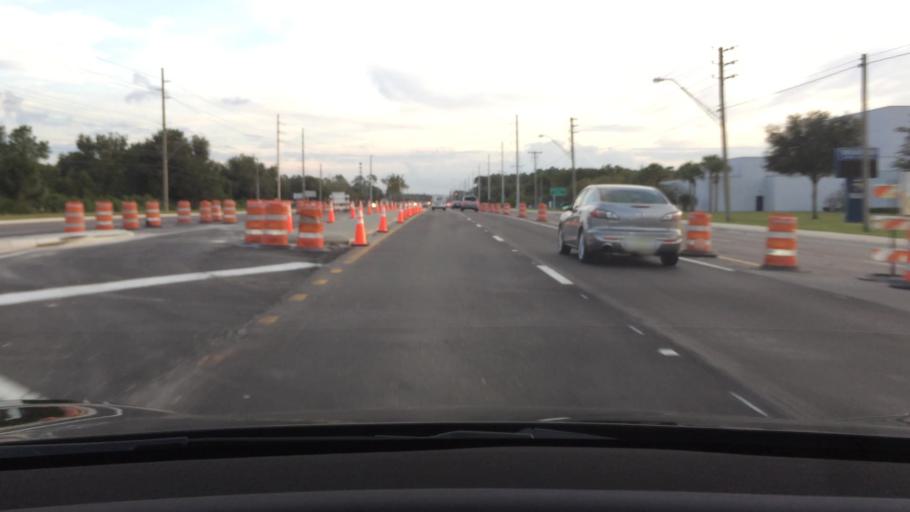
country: US
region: Florida
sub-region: Hillsborough County
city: Pebble Creek
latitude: 28.1589
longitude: -82.3535
